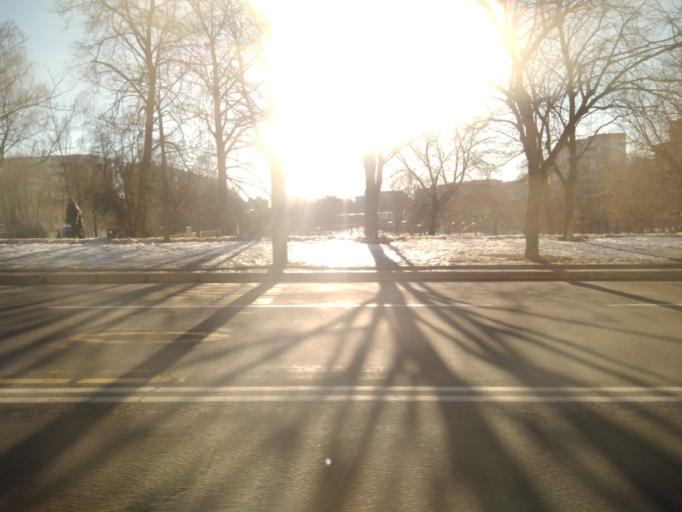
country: BY
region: Minsk
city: Minsk
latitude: 53.9004
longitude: 27.5848
